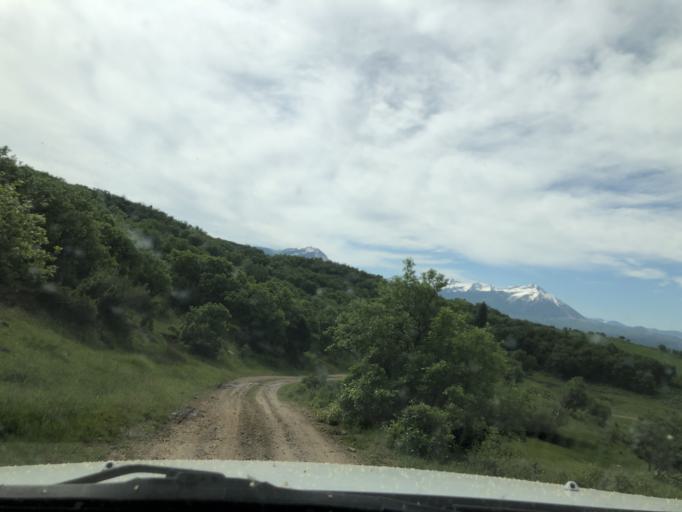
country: US
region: Colorado
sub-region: Delta County
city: Paonia
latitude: 39.0166
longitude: -107.3411
